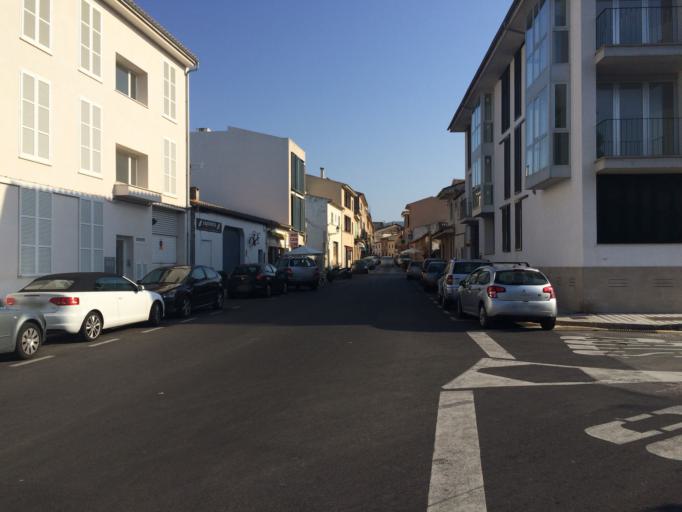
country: ES
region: Balearic Islands
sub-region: Illes Balears
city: Pollenca
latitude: 39.8820
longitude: 3.0195
